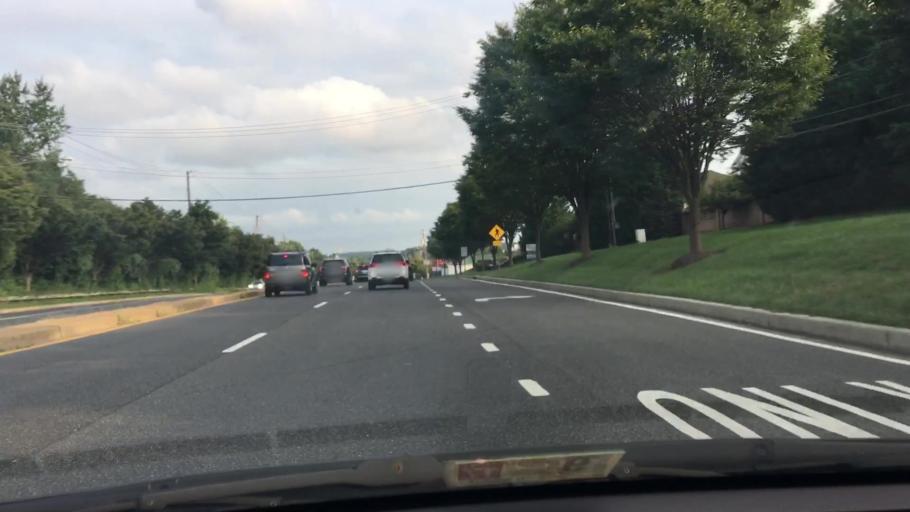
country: US
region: Maryland
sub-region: Montgomery County
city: Germantown
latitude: 39.1915
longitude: -77.2424
